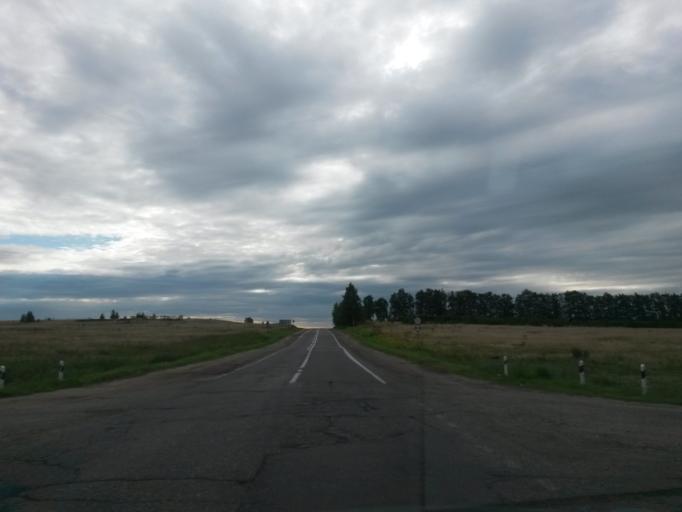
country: RU
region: Jaroslavl
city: Gavrilov-Yam
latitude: 57.3600
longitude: 39.7709
